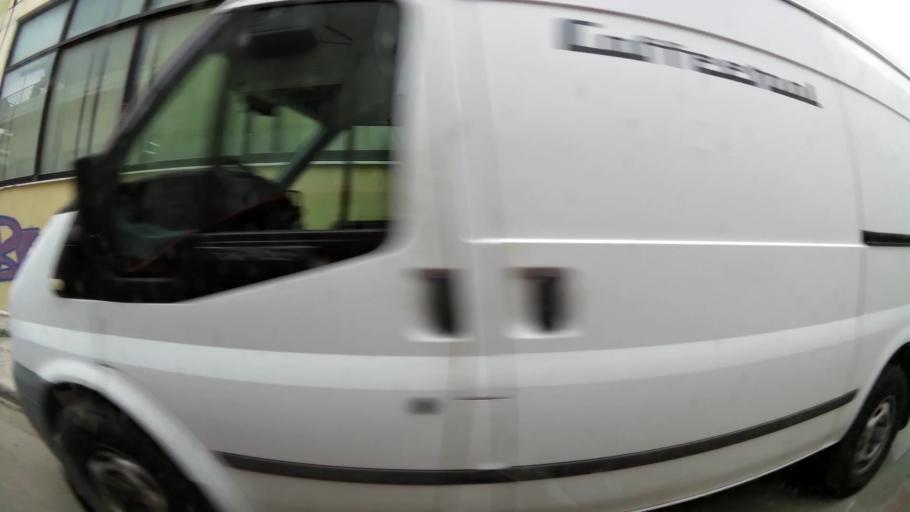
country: GR
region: Attica
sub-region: Nomarchia Athinas
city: Peristeri
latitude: 38.0016
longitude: 23.6960
